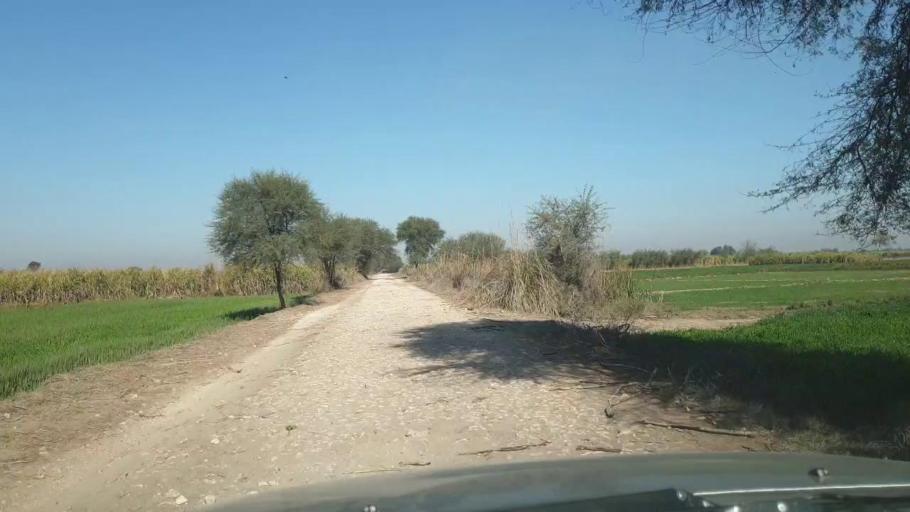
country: PK
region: Sindh
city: Ghotki
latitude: 28.0886
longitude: 69.3438
